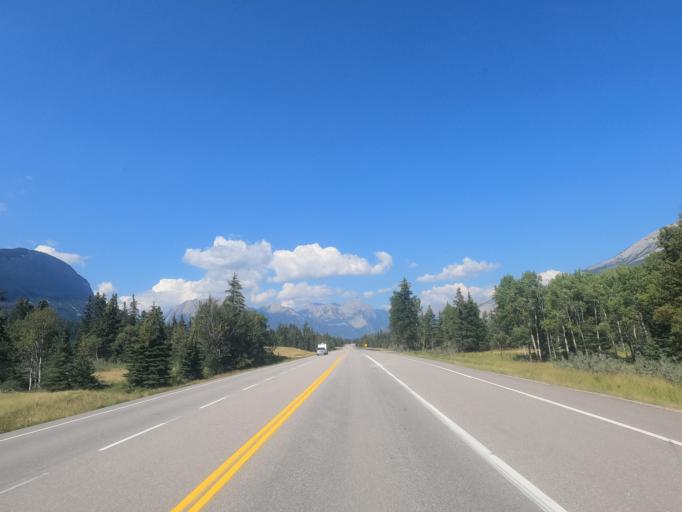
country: CA
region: Alberta
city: Jasper Park Lodge
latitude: 52.9616
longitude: -118.0501
